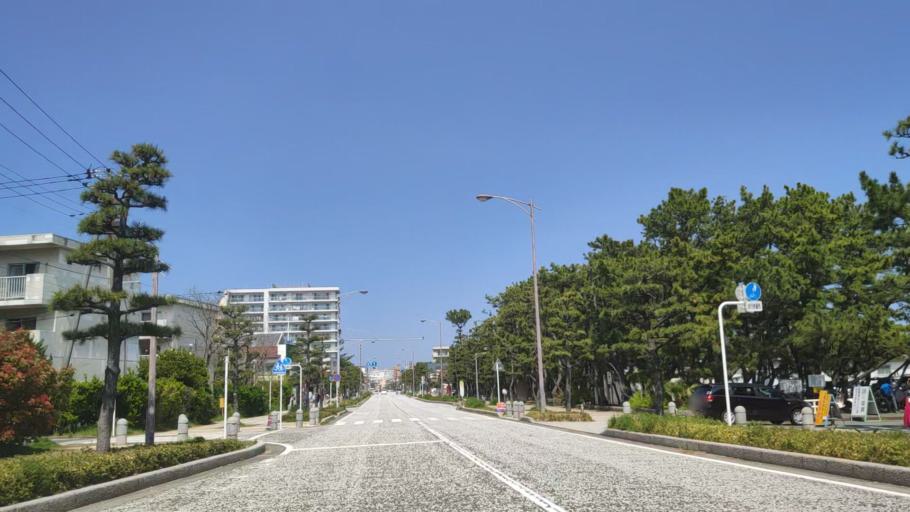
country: JP
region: Kanagawa
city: Hiratsuka
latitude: 35.3169
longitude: 139.3539
